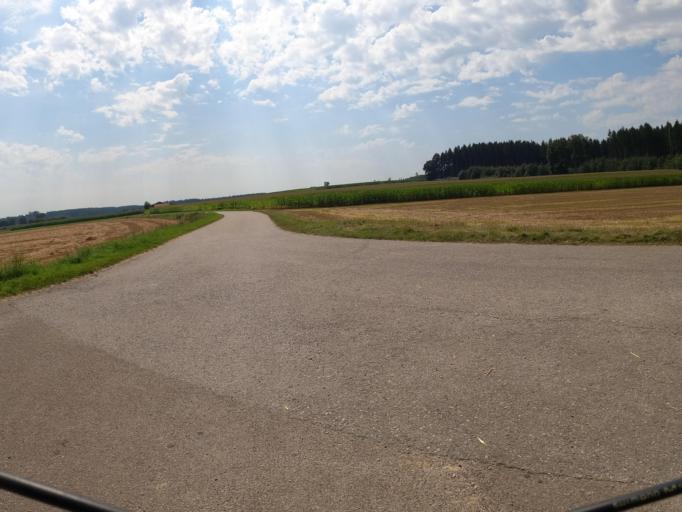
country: DE
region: Bavaria
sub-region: Swabia
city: Rieden an der Kotz
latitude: 48.3653
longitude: 10.2404
